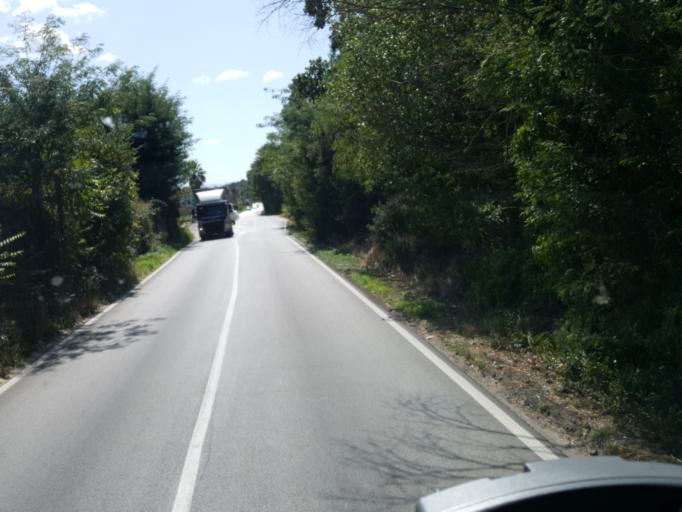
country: IT
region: Latium
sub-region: Provincia di Latina
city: Priverno
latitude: 41.4360
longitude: 13.1912
